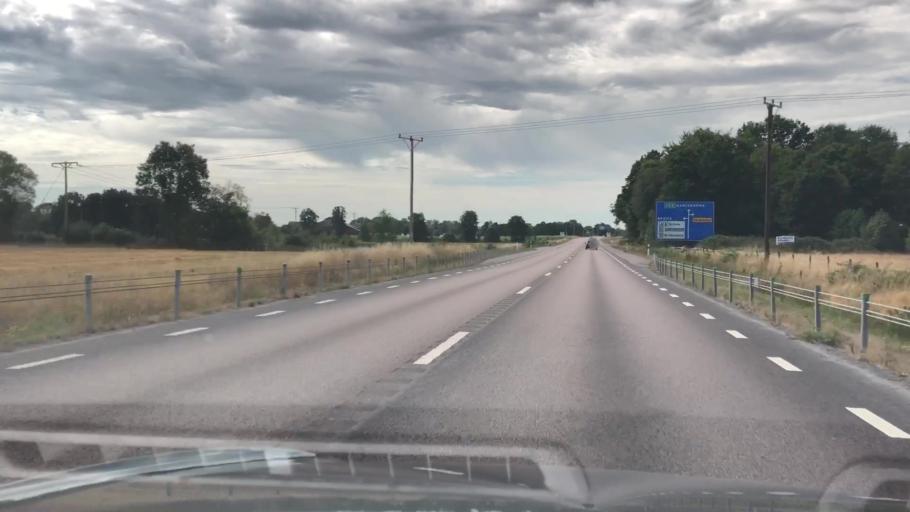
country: SE
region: Kalmar
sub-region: Torsas Kommun
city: Torsas
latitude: 56.3273
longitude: 16.0392
